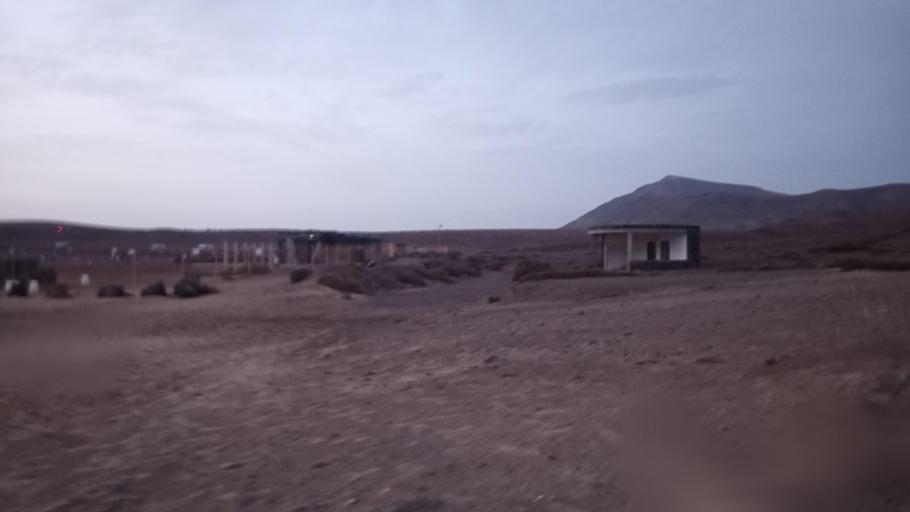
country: ES
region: Canary Islands
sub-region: Provincia de Las Palmas
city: Playa Blanca
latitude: 28.8443
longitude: -13.7811
